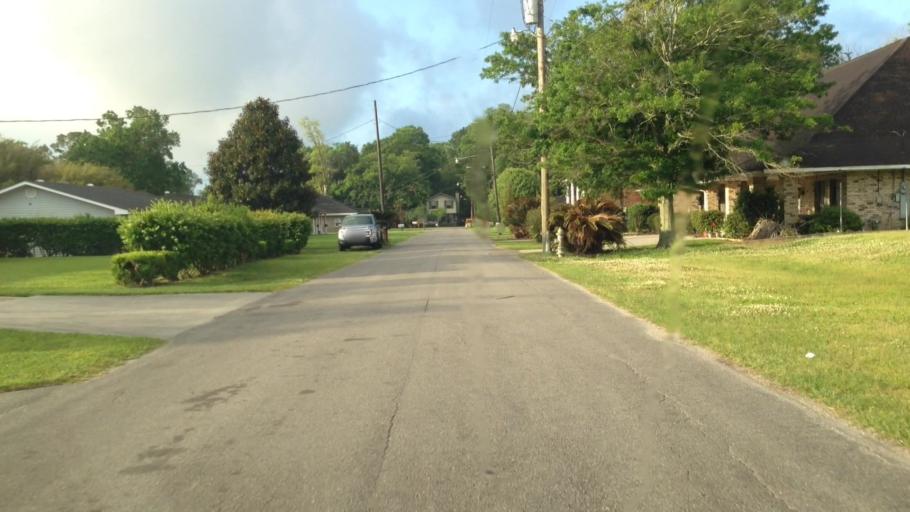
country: US
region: Louisiana
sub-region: Jefferson Parish
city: Jefferson
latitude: 29.9511
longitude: -90.1512
